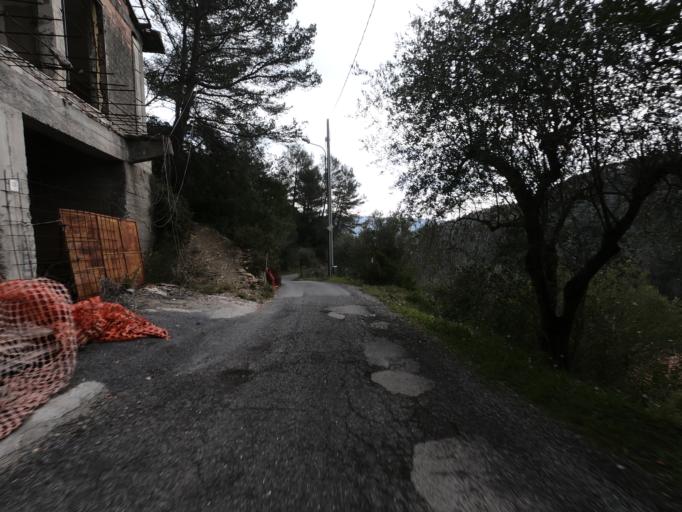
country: IT
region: Liguria
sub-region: Provincia di Imperia
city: Villa Faraldi
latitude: 43.9930
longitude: 8.1060
